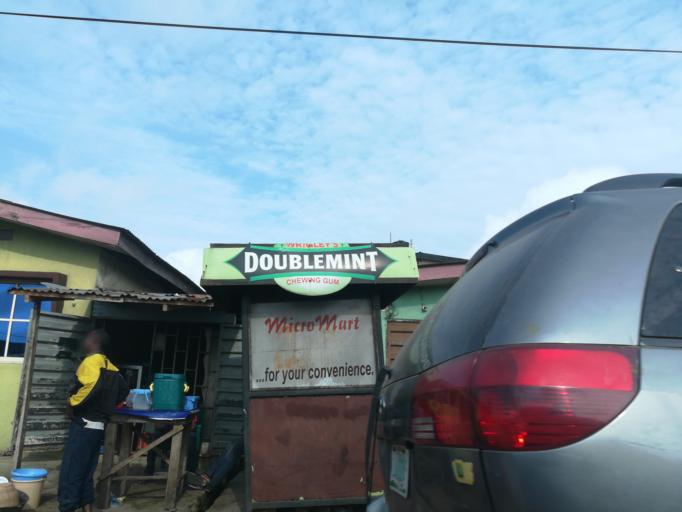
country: NG
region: Lagos
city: Agege
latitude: 6.6155
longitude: 3.3137
